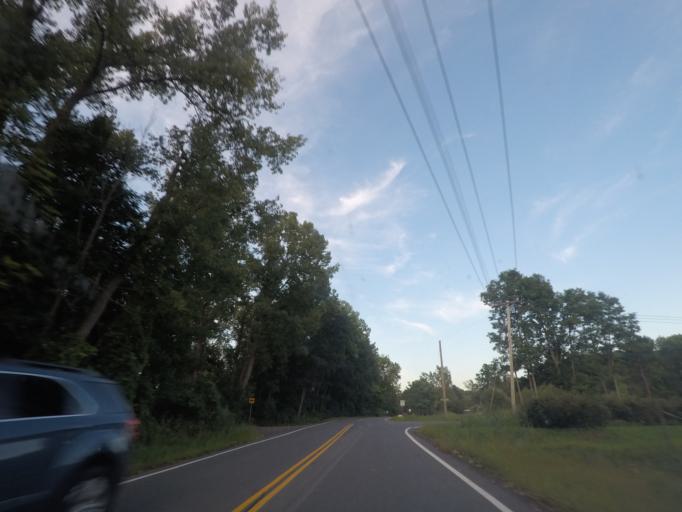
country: US
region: New York
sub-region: Schenectady County
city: Niskayuna
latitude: 42.7707
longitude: -73.8075
